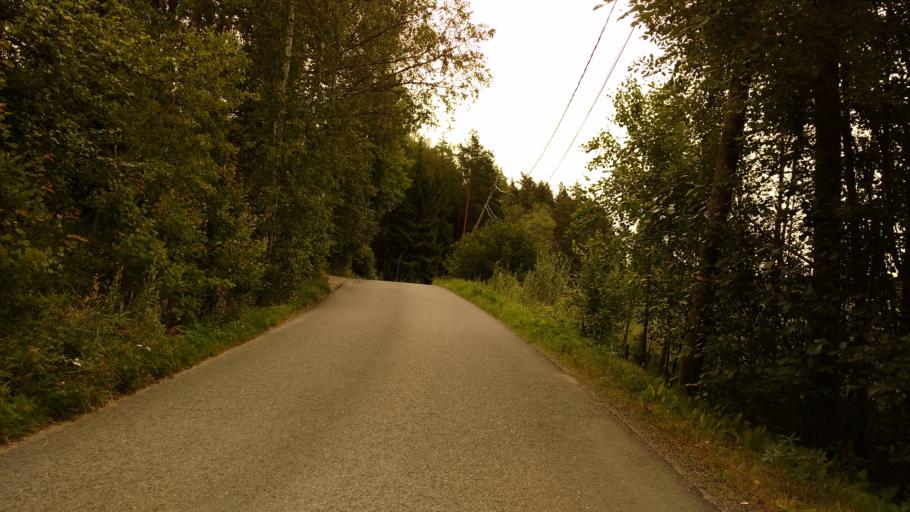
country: FI
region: Varsinais-Suomi
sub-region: Turku
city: Lieto
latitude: 60.4399
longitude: 22.4389
